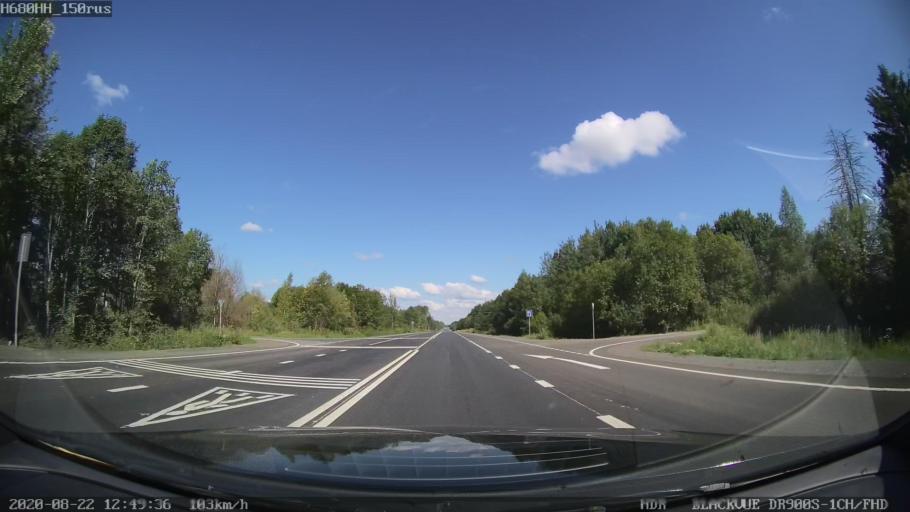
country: RU
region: Tverskaya
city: Rameshki
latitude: 57.4540
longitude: 36.2081
